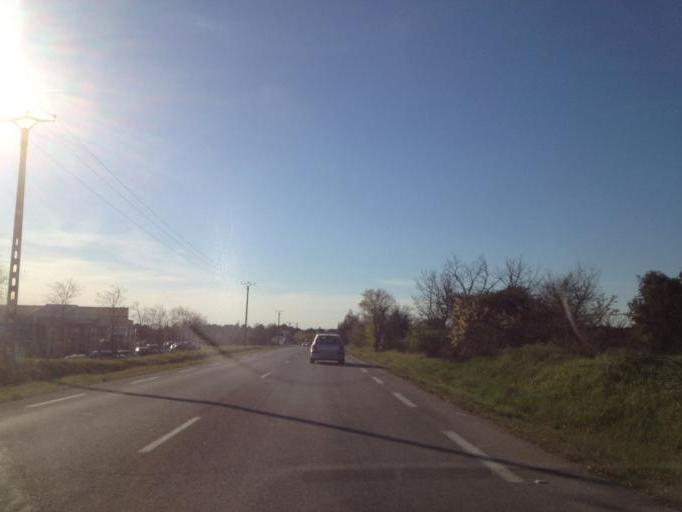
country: FR
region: Provence-Alpes-Cote d'Azur
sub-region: Departement des Bouches-du-Rhone
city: Saint-Cannat
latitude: 43.6151
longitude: 5.3190
